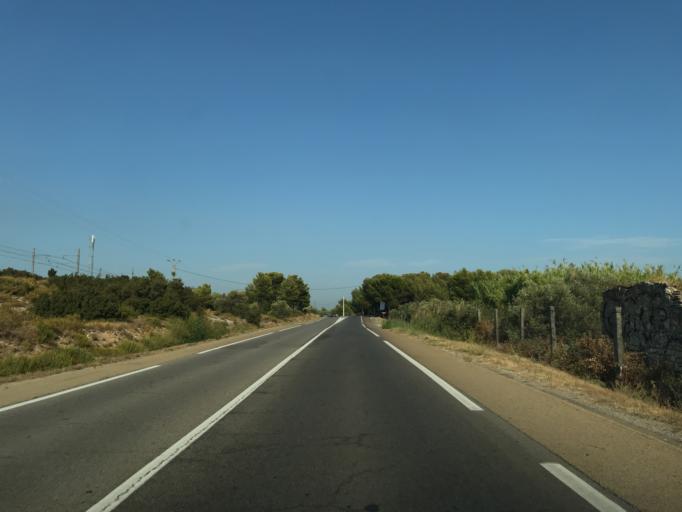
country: FR
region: Provence-Alpes-Cote d'Azur
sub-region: Departement des Bouches-du-Rhone
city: Cornillon-Confoux
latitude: 43.5277
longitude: 5.0906
